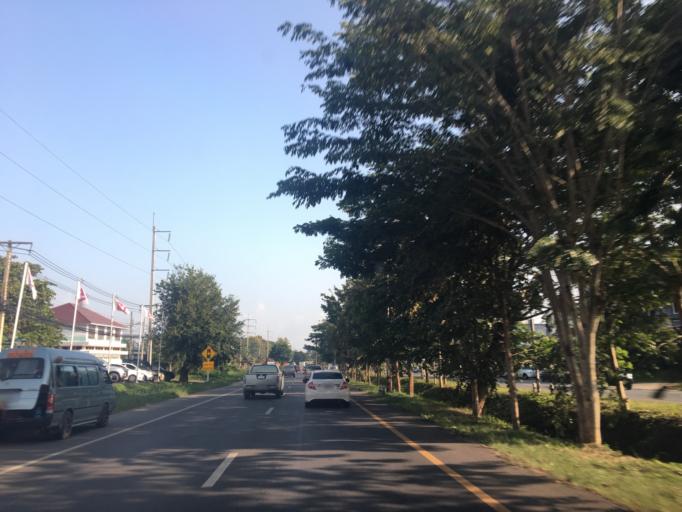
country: TH
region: Phayao
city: Phayao
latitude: 19.1682
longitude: 99.9090
